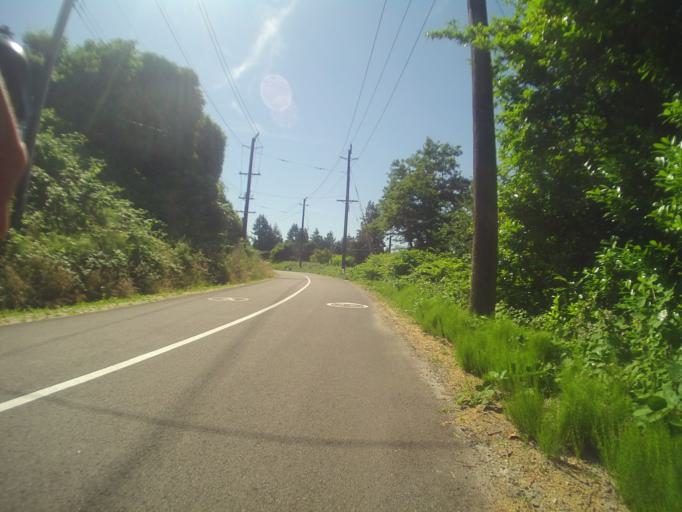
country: CA
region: British Columbia
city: Vancouver
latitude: 49.2408
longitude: -123.1521
